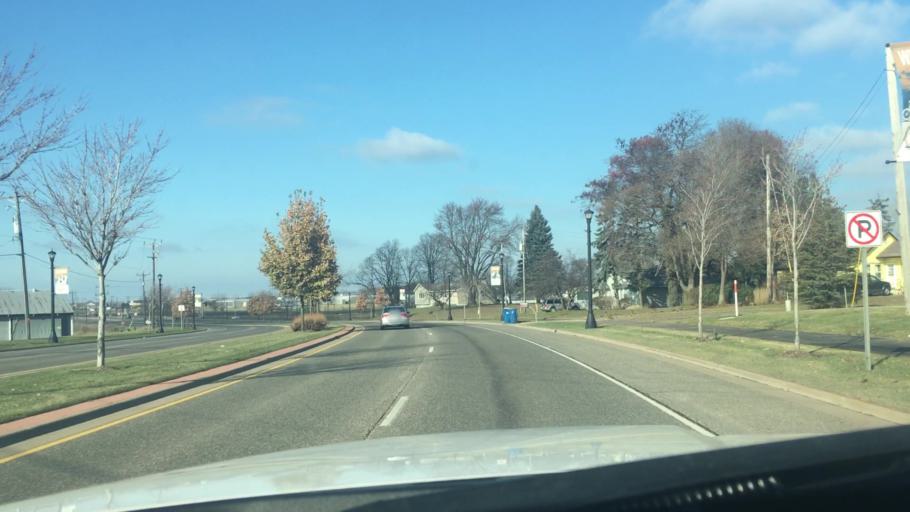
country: US
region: Minnesota
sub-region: Washington County
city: Hugo
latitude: 45.1601
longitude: -92.9997
